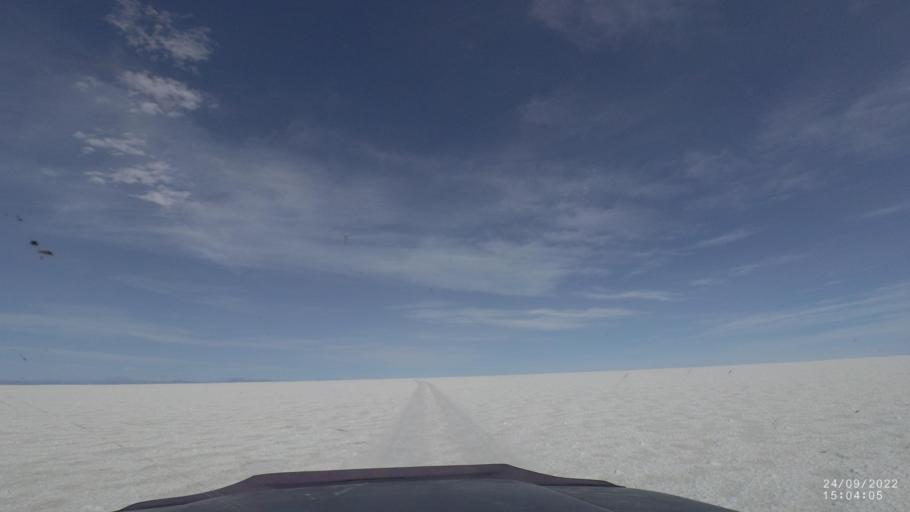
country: BO
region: Potosi
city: Colchani
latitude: -19.8983
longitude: -67.5262
